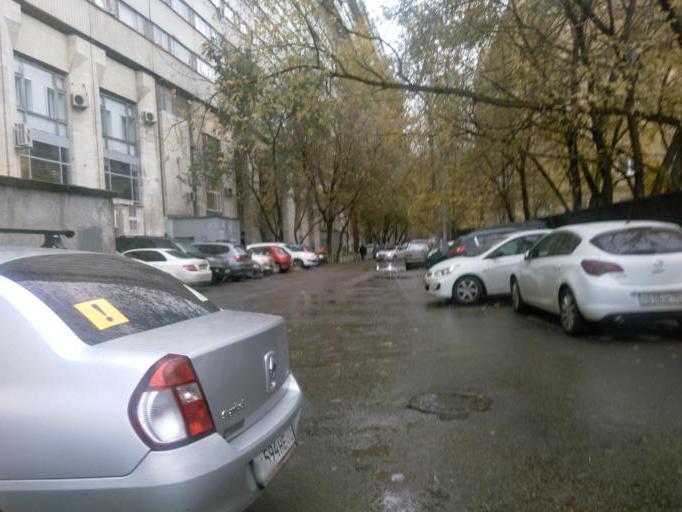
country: RU
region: Moscow
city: Zamoskvorech'ye
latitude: 55.7094
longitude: 37.6205
